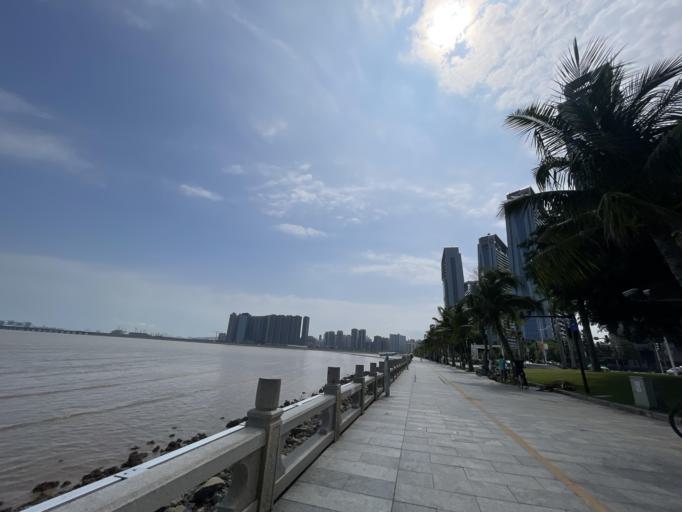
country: MO
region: Macau
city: Macau
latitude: 22.2262
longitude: 113.5570
